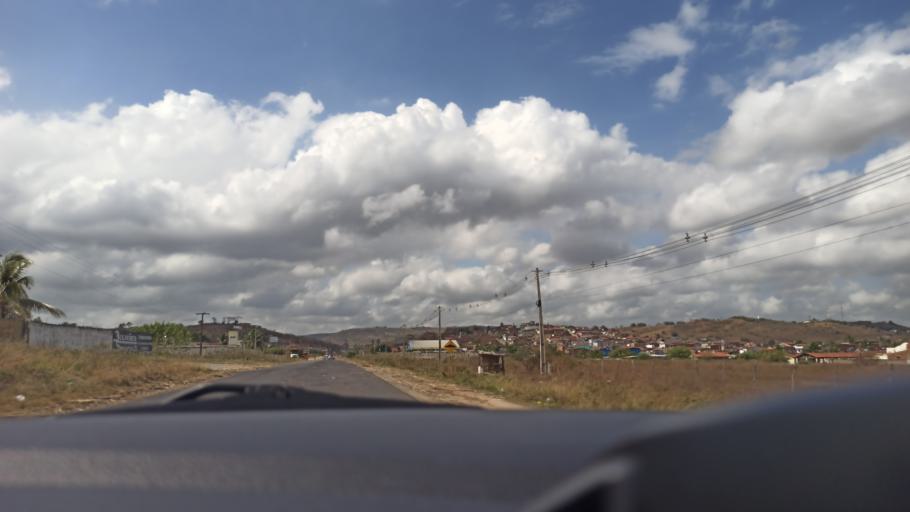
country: BR
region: Pernambuco
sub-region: Timbauba
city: Timbauba
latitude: -7.4965
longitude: -35.2977
